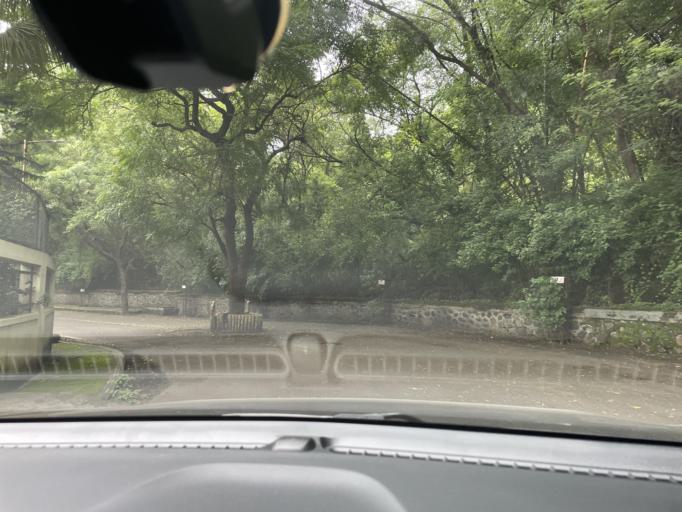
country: IN
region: Maharashtra
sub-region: Pune Division
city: Shivaji Nagar
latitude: 18.5301
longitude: 73.8151
